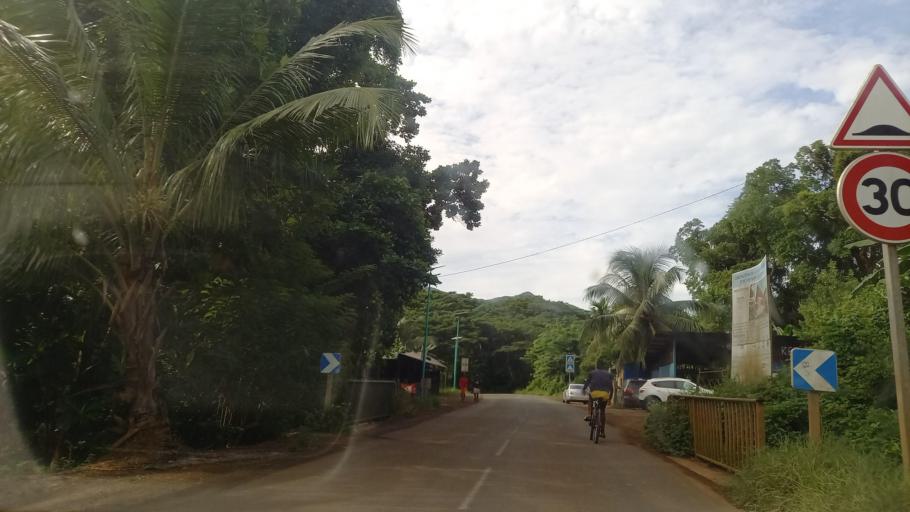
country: YT
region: Chirongui
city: Chirongui
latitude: -12.9191
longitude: 45.1591
